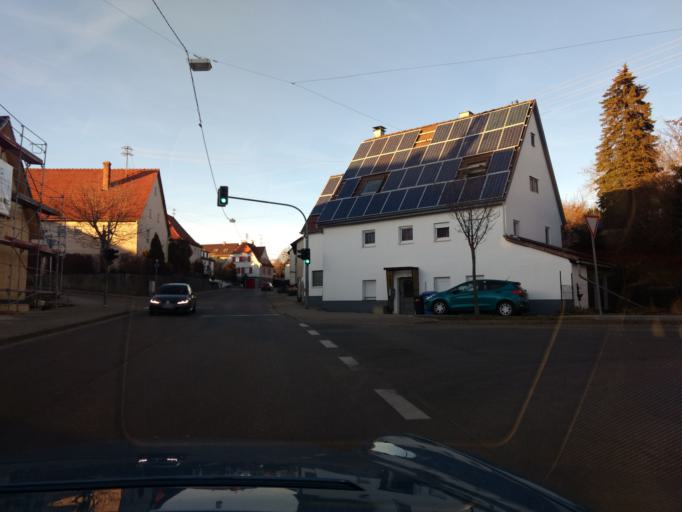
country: DE
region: Baden-Wuerttemberg
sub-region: Regierungsbezirk Stuttgart
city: Schwabisch Gmund
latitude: 48.7802
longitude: 9.7963
